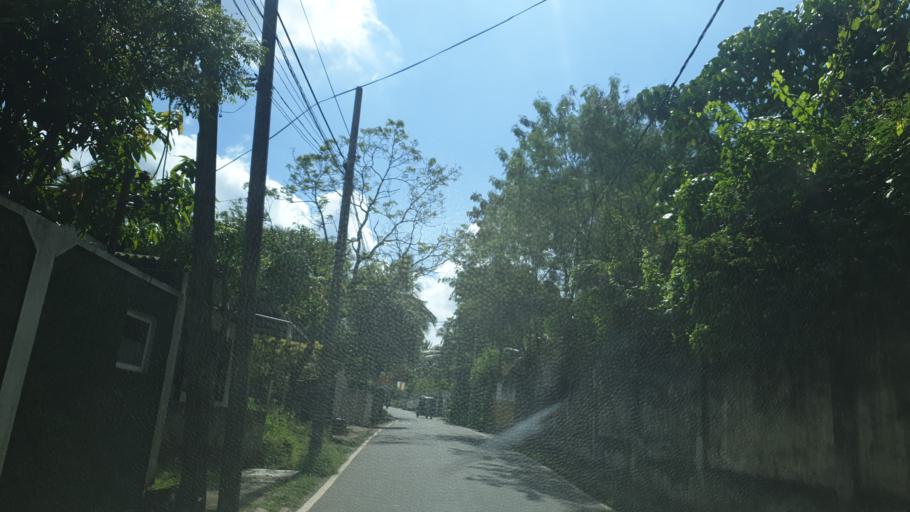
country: LK
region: Western
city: Moratuwa
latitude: 6.7938
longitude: 79.9095
